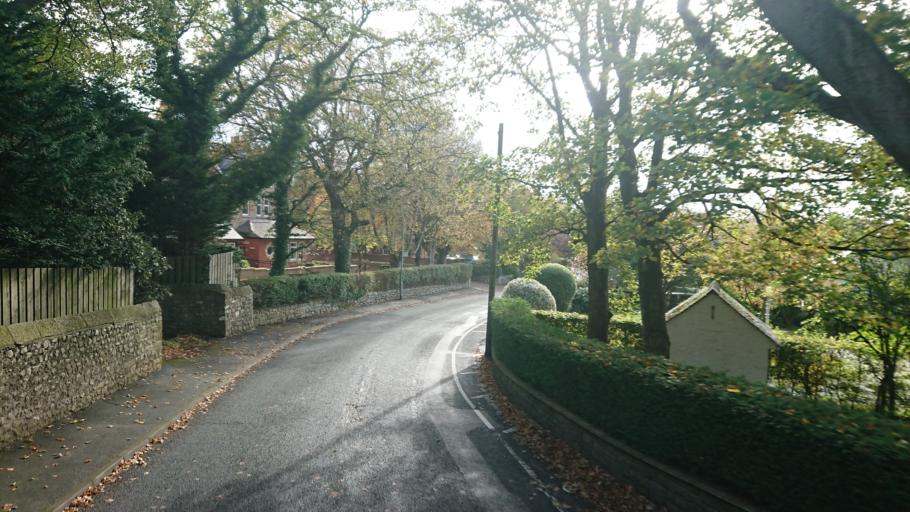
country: GB
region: England
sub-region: Lancashire
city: Bolton le Sands
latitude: 54.0882
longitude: -2.8106
